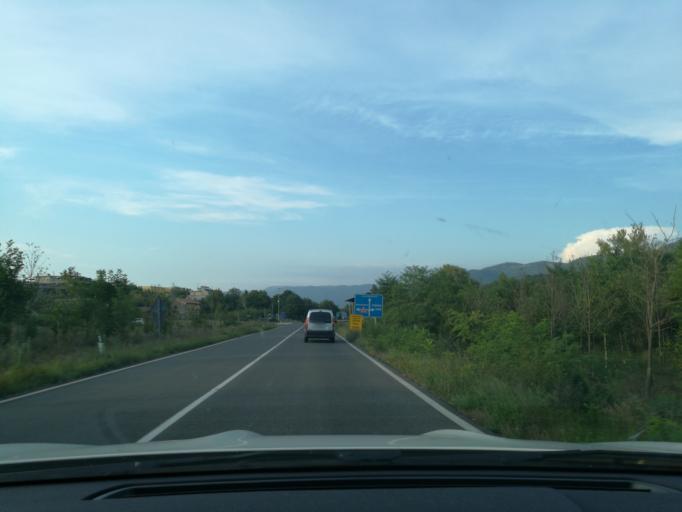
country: IT
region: Umbria
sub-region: Provincia di Terni
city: Acquasparta
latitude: 42.6551
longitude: 12.5357
